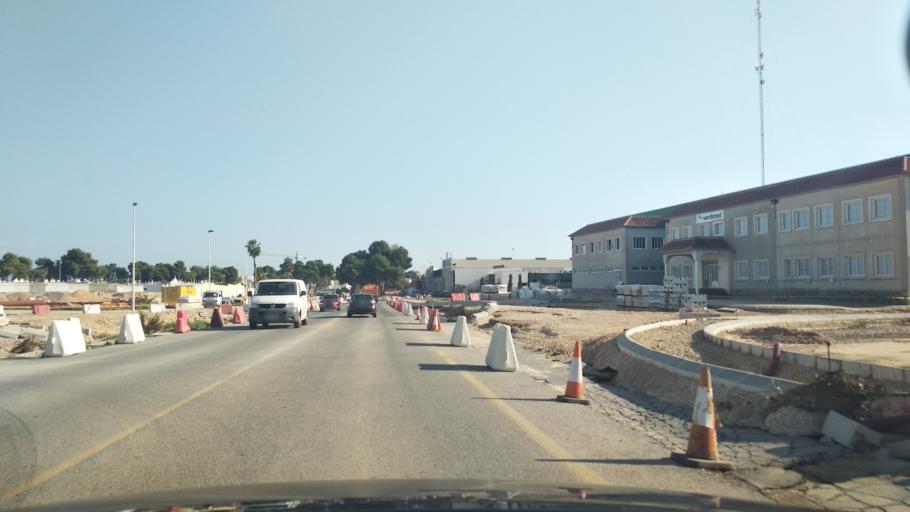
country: ES
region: Murcia
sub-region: Murcia
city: San Javier
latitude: 37.8126
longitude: -0.8394
